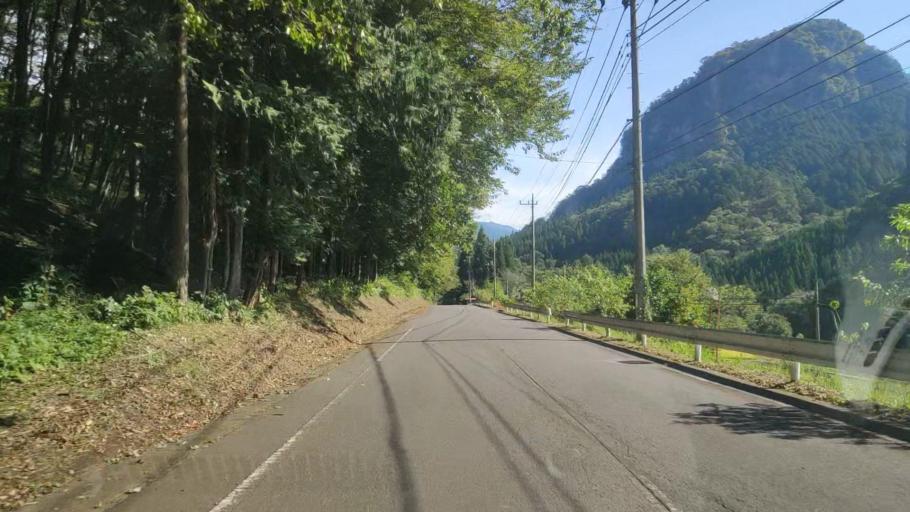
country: JP
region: Gunma
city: Nakanojomachi
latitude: 36.6108
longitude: 138.7370
